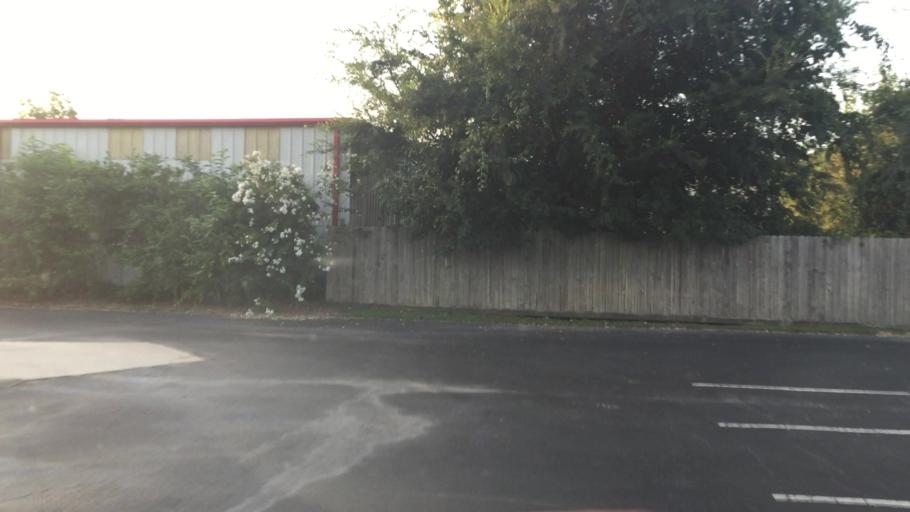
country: US
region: Texas
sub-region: Harris County
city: Hudson
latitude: 29.9907
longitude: -95.5022
